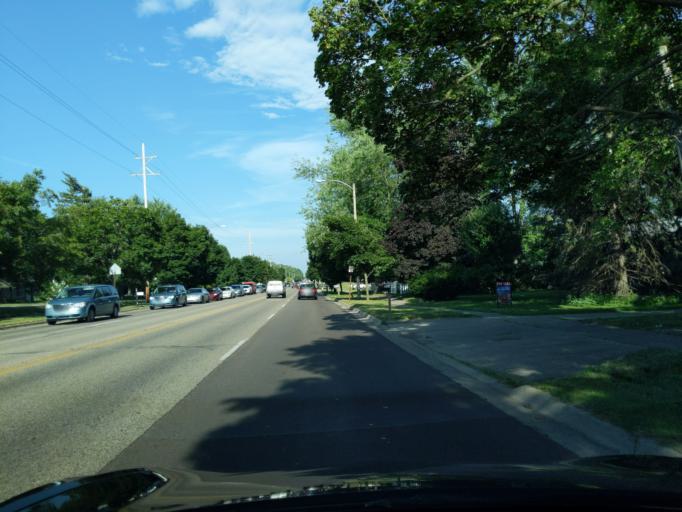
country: US
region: Michigan
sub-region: Ingham County
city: East Lansing
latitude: 42.7470
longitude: -84.4602
